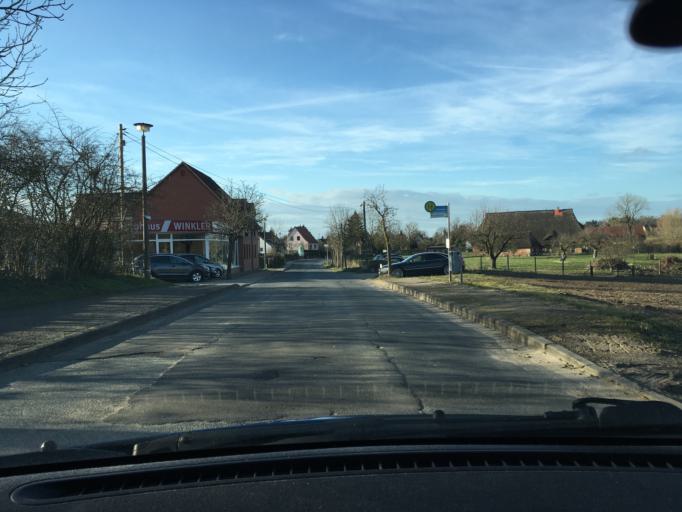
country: DE
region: Mecklenburg-Vorpommern
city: Feldstadt
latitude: 53.5941
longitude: 11.4060
